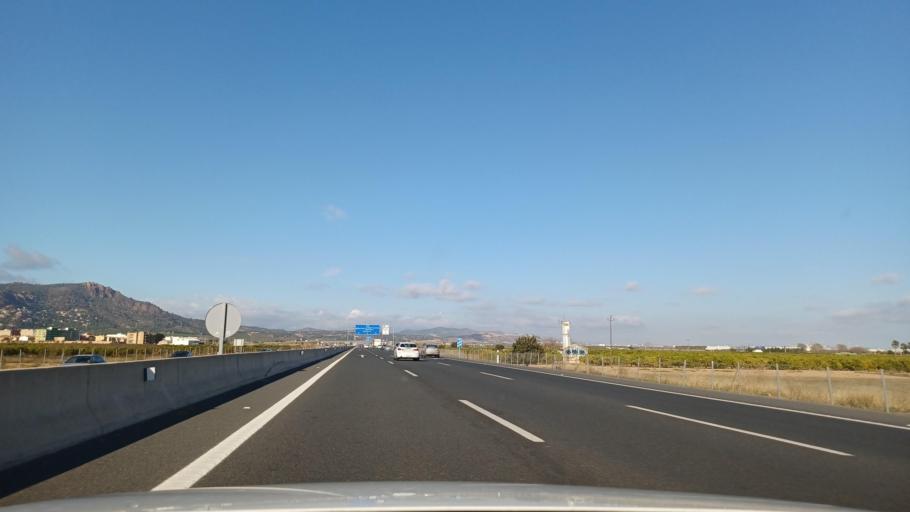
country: ES
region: Valencia
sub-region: Provincia de Valencia
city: Pucol
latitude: 39.6072
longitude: -0.2940
